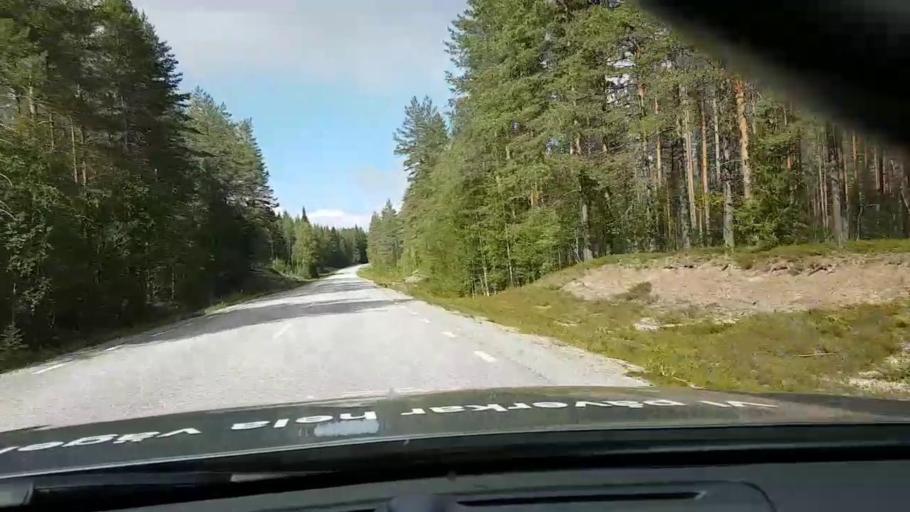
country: SE
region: Vaesternorrland
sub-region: OErnskoeldsviks Kommun
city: Bredbyn
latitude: 63.6921
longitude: 17.7685
